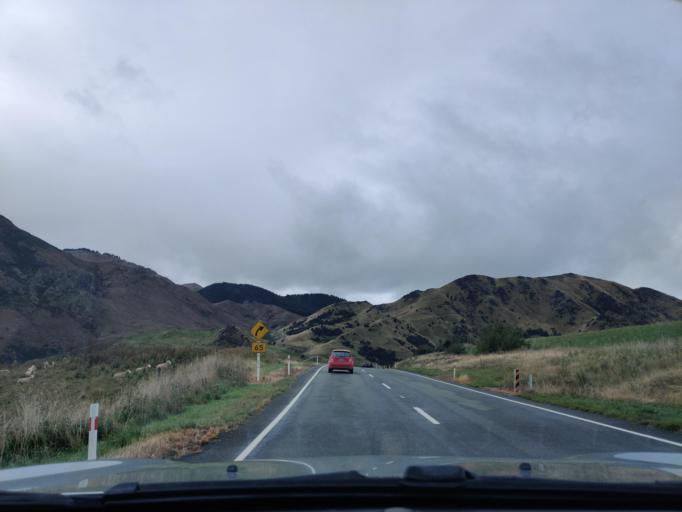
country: NZ
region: Canterbury
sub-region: Hurunui District
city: Amberley
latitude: -42.6412
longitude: 172.7714
